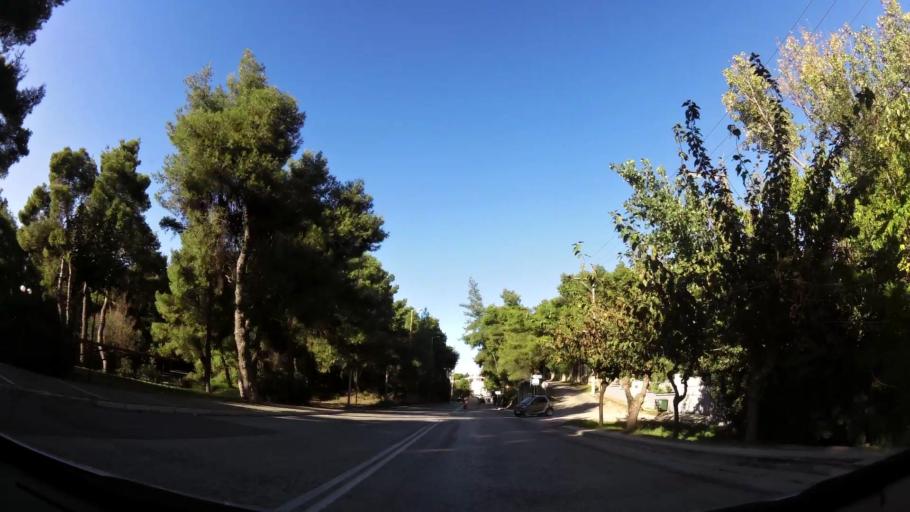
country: GR
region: Attica
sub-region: Nomarchia Anatolikis Attikis
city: Anoixi
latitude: 38.1261
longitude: 23.8566
